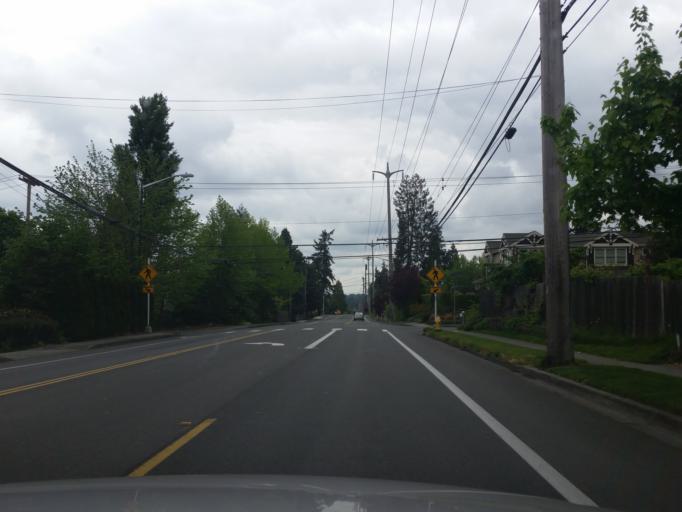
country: US
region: Washington
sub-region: King County
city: Kirkland
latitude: 47.6605
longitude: -122.1961
